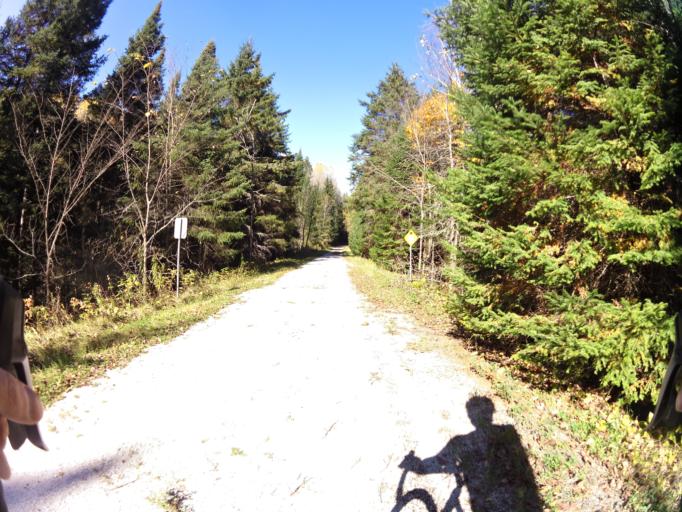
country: CA
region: Quebec
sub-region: Outaouais
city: Wakefield
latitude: 45.8527
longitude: -75.9917
